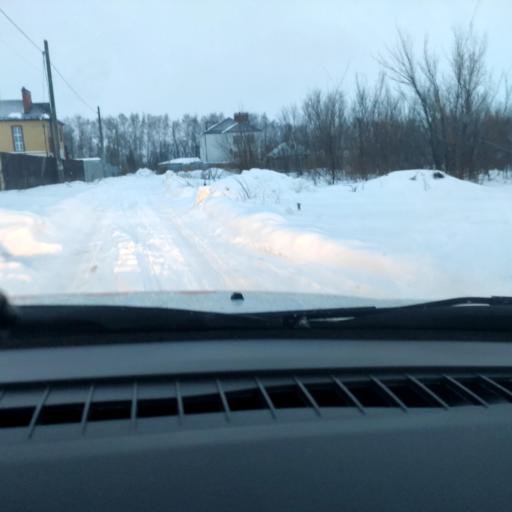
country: RU
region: Samara
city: Dubovyy Umet
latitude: 53.0300
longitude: 50.2300
